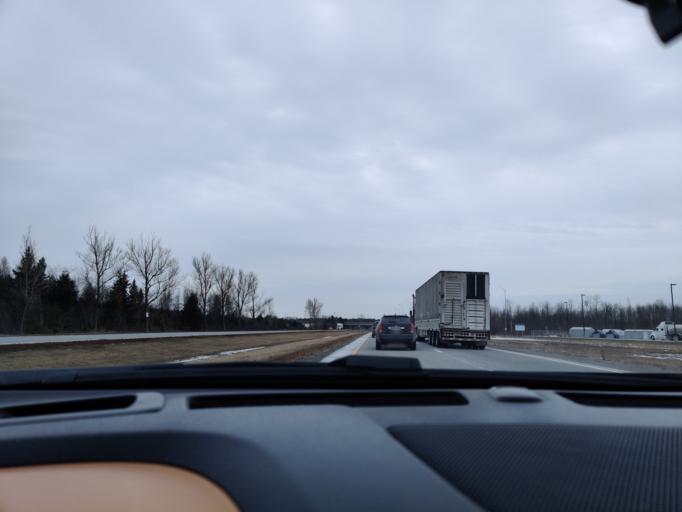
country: US
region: New York
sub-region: St. Lawrence County
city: Norfolk
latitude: 44.9716
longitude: -75.0801
